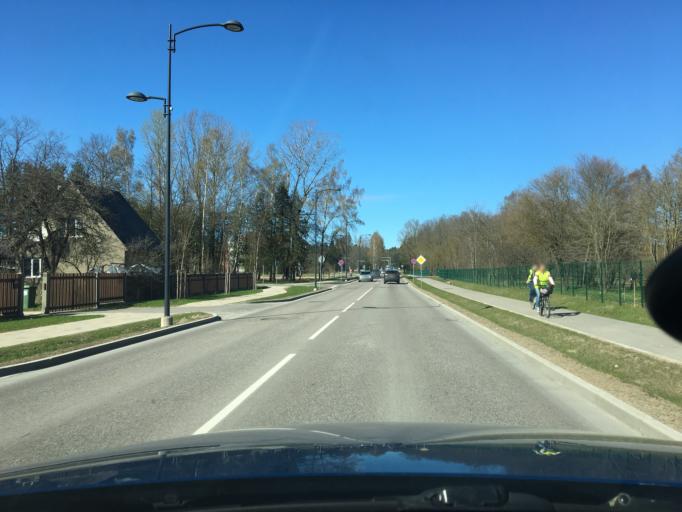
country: LV
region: Salaspils
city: Salaspils
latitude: 56.8666
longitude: 24.3519
